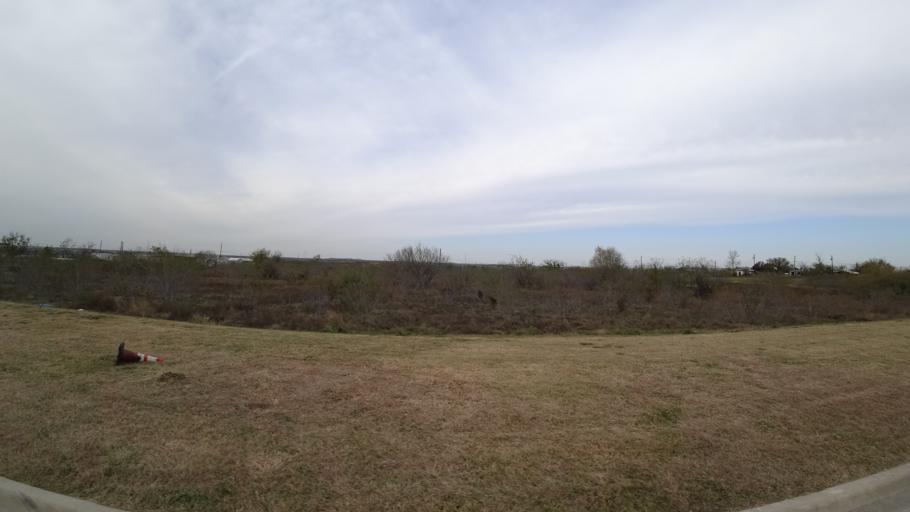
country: US
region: Texas
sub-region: Travis County
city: Garfield
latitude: 30.1430
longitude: -97.6255
